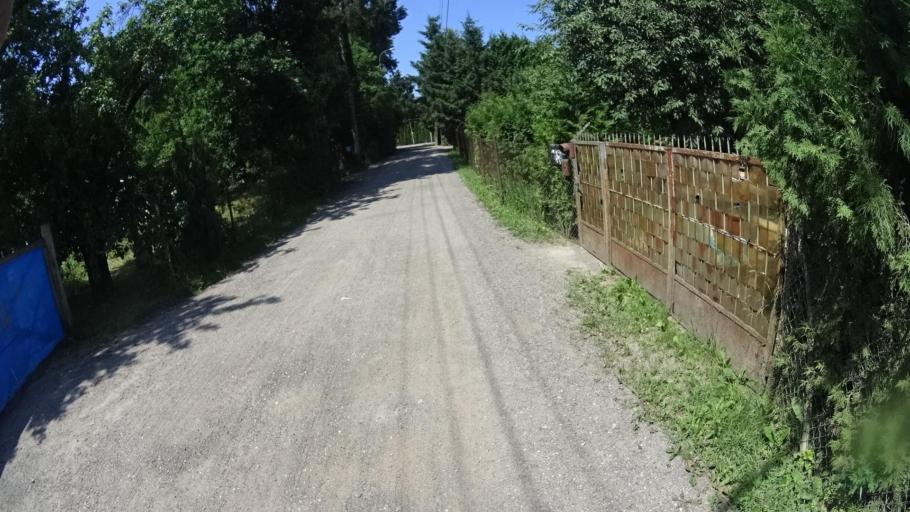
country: PL
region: Masovian Voivodeship
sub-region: Warszawa
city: Bialoleka
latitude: 52.3409
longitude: 20.9428
